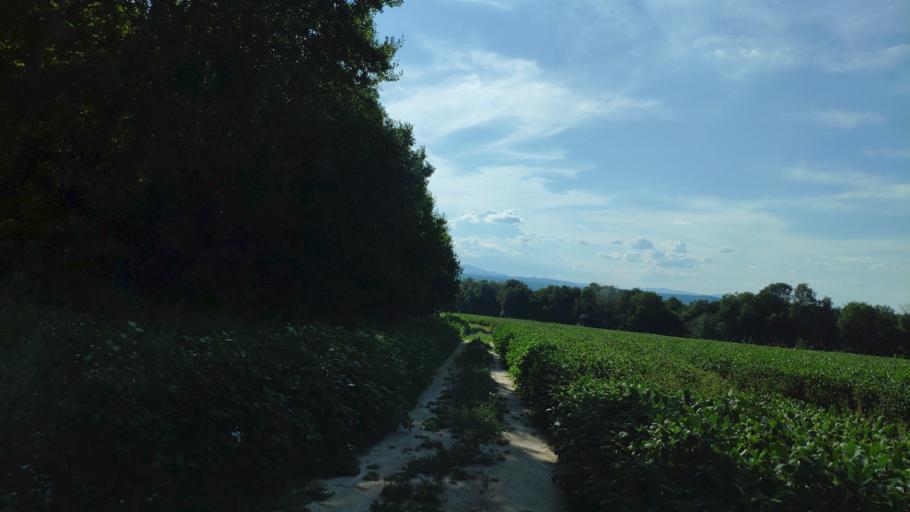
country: SK
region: Presovsky
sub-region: Okres Presov
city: Presov
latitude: 48.9073
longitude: 21.2906
